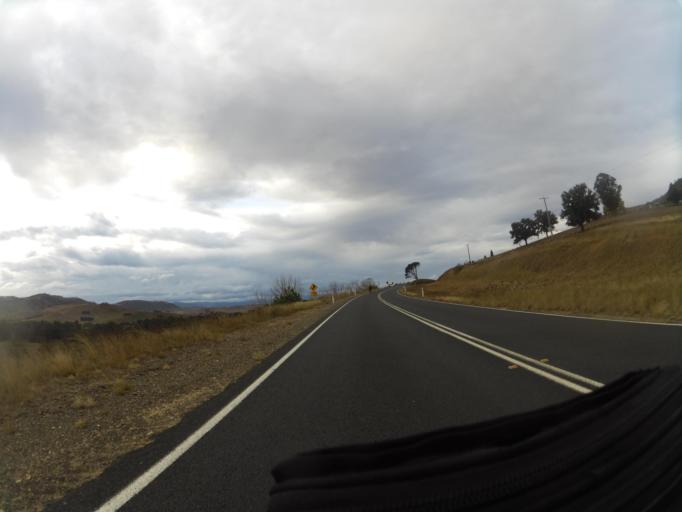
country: AU
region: New South Wales
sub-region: Snowy River
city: Jindabyne
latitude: -36.0837
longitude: 147.9775
